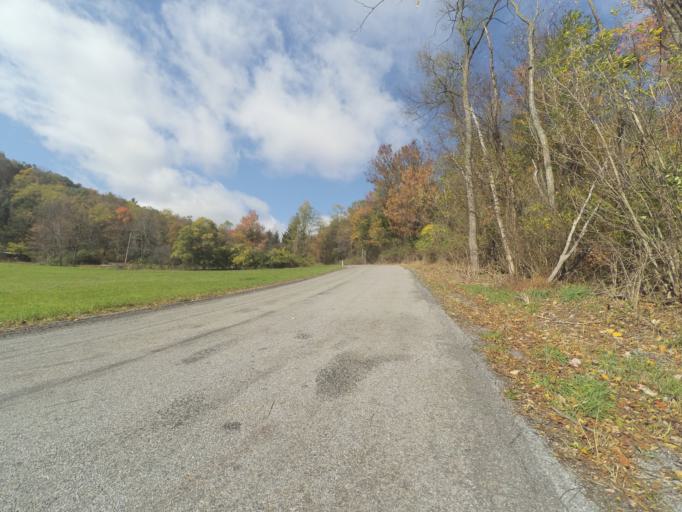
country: US
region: Pennsylvania
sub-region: Centre County
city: Stormstown
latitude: 40.8759
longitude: -77.9959
